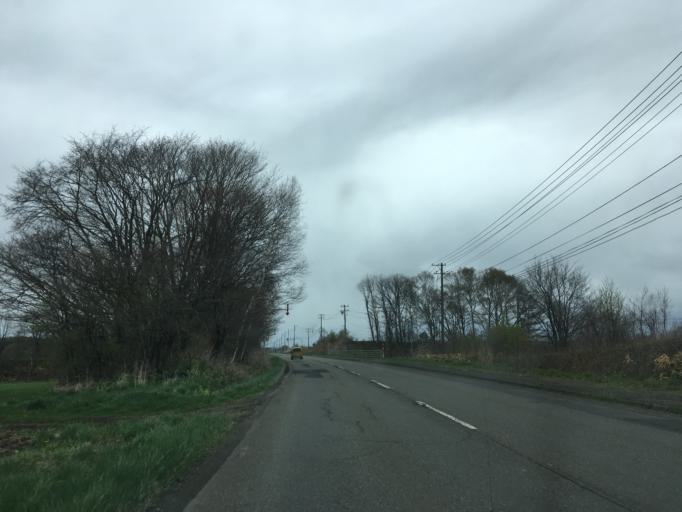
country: JP
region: Hokkaido
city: Chitose
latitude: 42.8990
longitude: 141.8138
